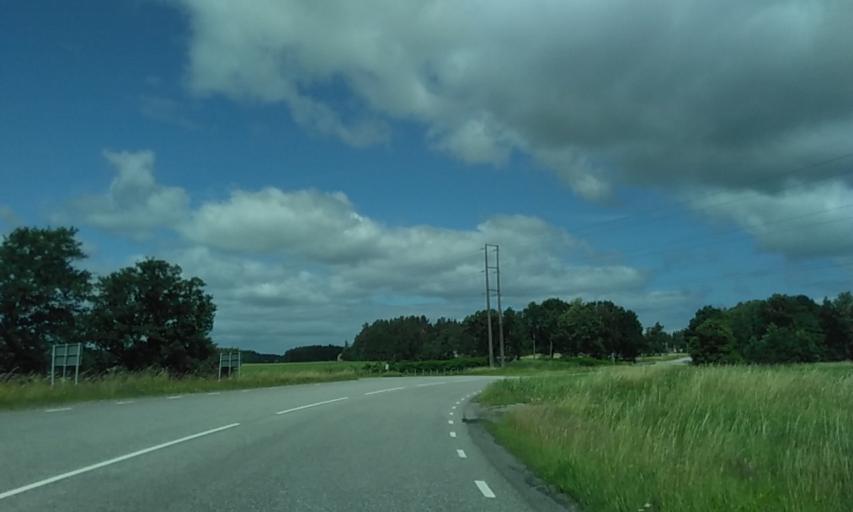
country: SE
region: Vaestra Goetaland
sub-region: Grastorps Kommun
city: Graestorp
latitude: 58.3427
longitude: 12.6853
